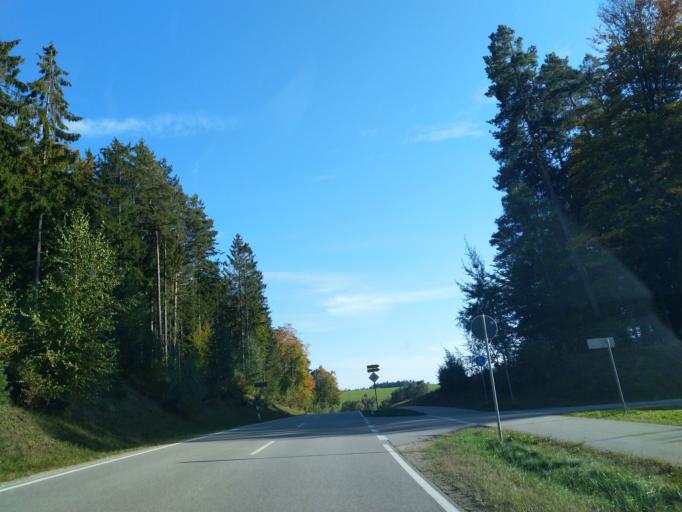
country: DE
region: Bavaria
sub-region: Lower Bavaria
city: Bernried
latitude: 48.9035
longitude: 12.8939
